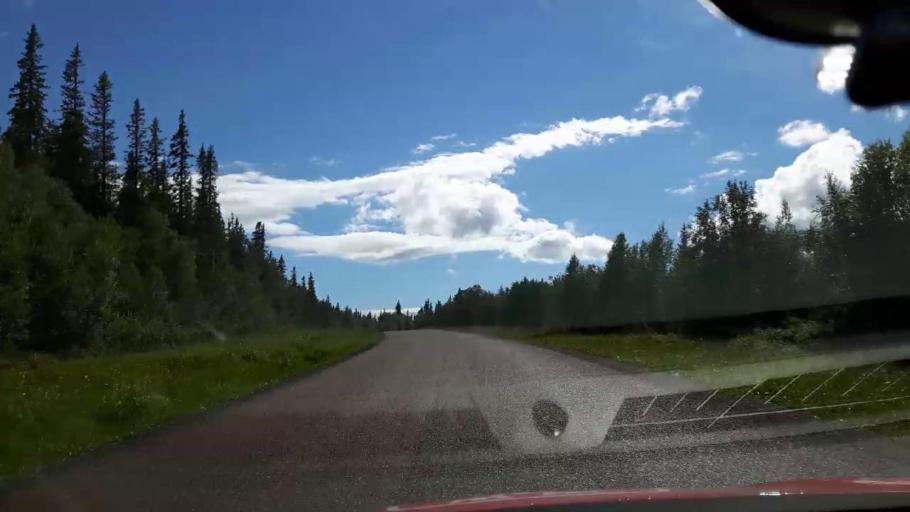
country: SE
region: Jaemtland
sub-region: Are Kommun
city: Are
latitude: 63.2697
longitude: 13.2204
